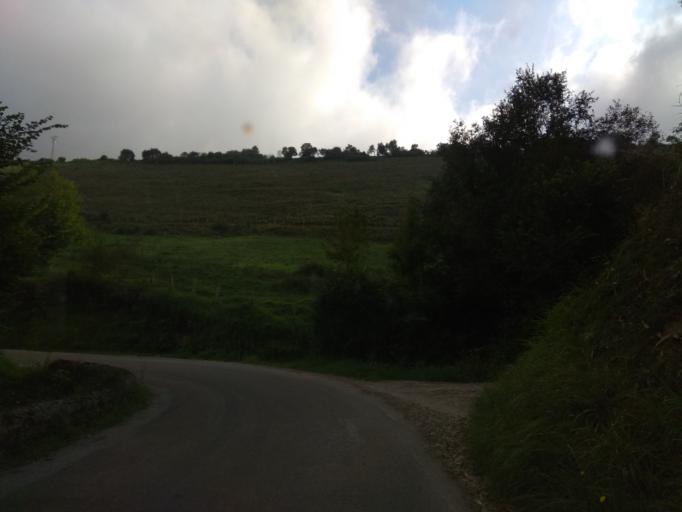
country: ES
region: Cantabria
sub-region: Provincia de Cantabria
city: San Vicente de la Barquera
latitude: 43.3146
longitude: -4.3917
